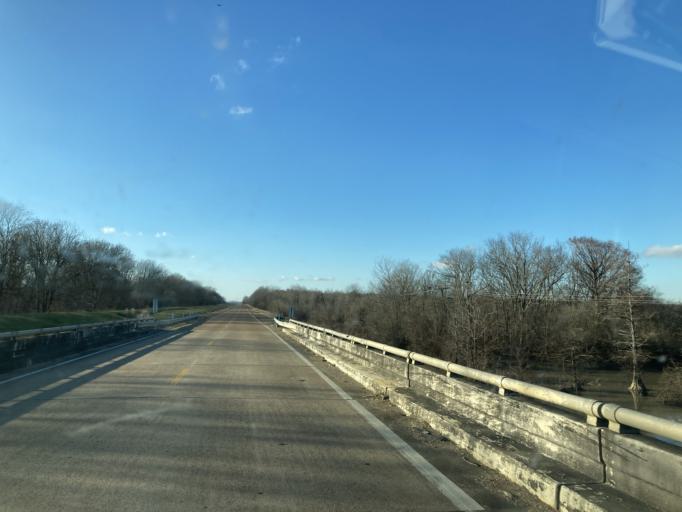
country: US
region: Mississippi
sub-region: Yazoo County
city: Yazoo City
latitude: 32.9189
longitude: -90.5579
